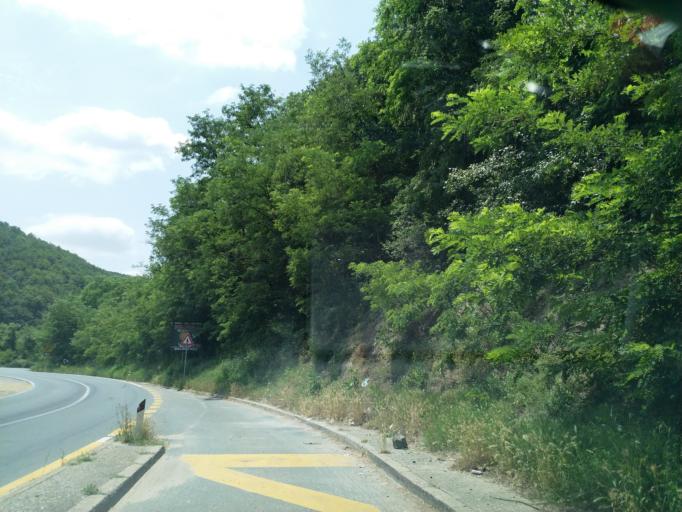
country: RS
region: Central Serbia
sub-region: Rasinski Okrug
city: Aleksandrovac
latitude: 43.4024
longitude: 21.1565
